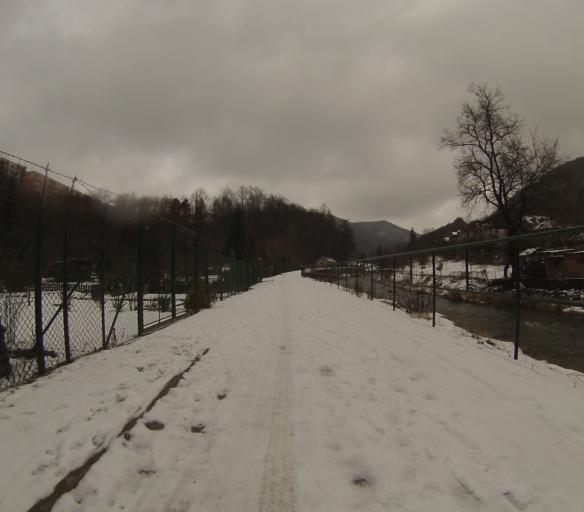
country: CZ
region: Ustecky
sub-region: Okres Decin
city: Decin
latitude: 50.7615
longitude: 14.2450
